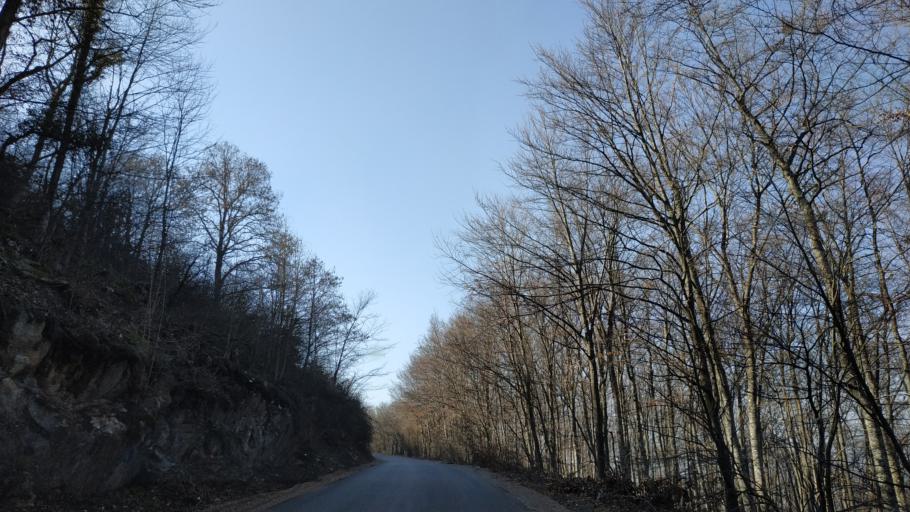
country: RS
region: Central Serbia
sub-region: Zajecarski Okrug
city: Soko Banja
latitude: 43.5991
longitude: 21.8868
